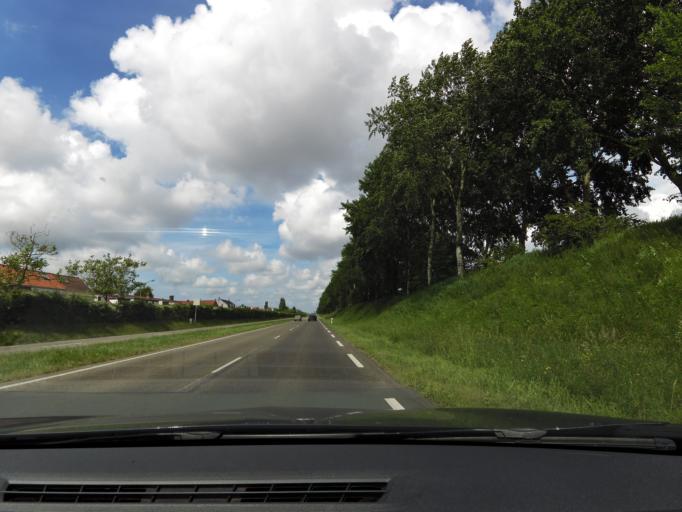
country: NL
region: Zeeland
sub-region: Gemeente Vlissingen
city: Vlissingen
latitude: 51.4674
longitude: 3.5947
